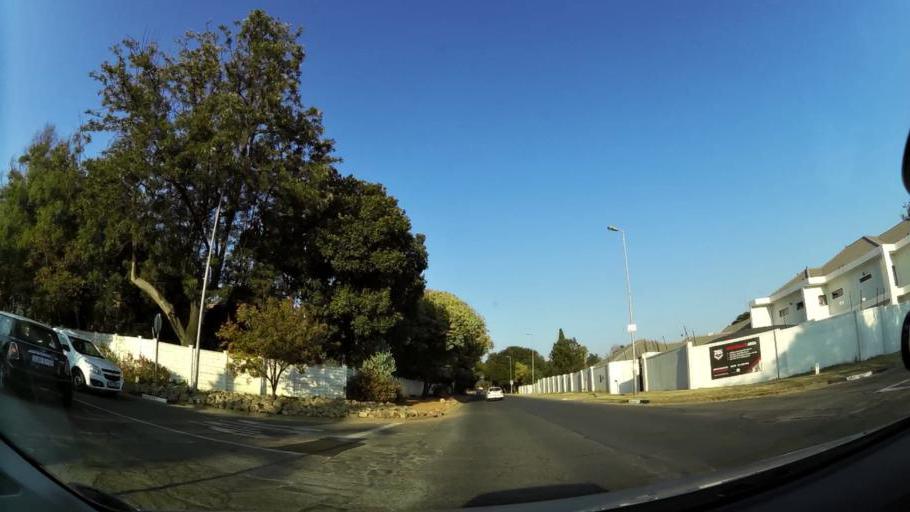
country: ZA
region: Gauteng
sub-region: City of Johannesburg Metropolitan Municipality
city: Modderfontein
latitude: -26.0768
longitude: 28.0989
